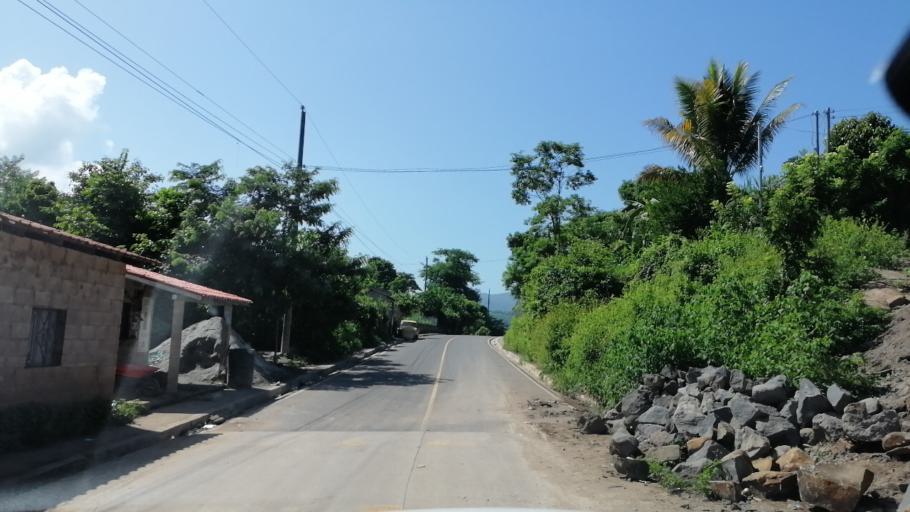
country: SV
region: Cabanas
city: Victoria
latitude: 13.9526
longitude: -88.7333
